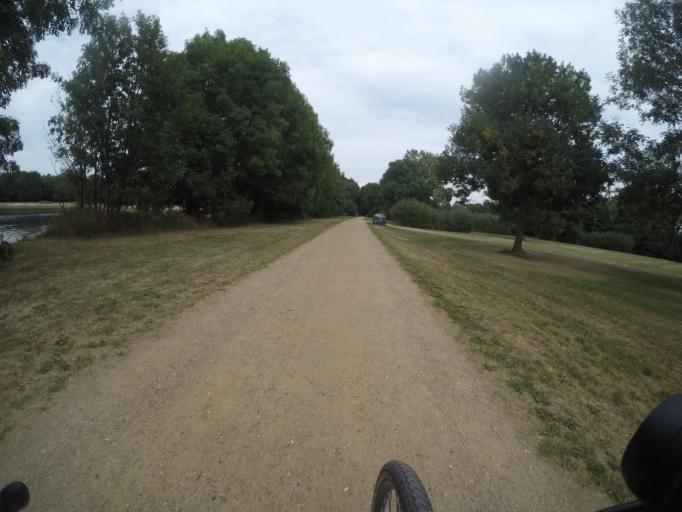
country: DE
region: Hamburg
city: Wandsbek
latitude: 53.4839
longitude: 10.1104
